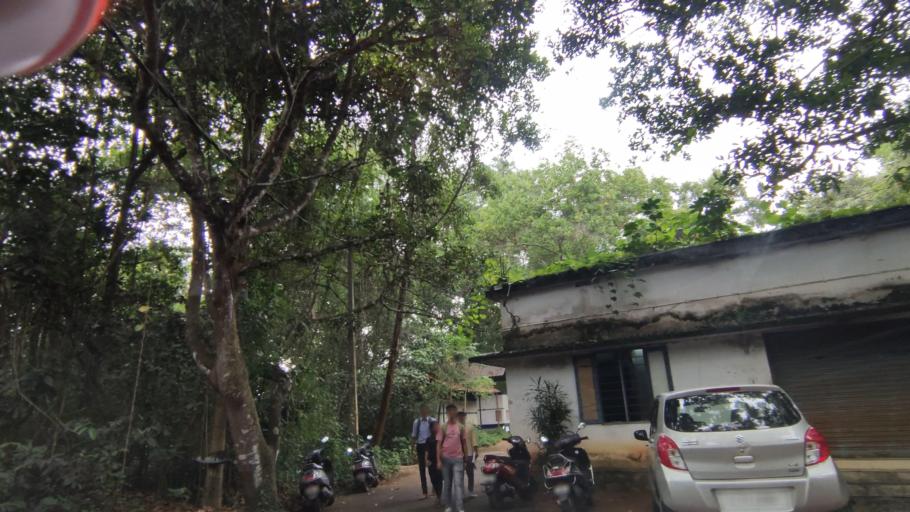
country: IN
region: Kerala
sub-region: Kottayam
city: Kottayam
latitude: 9.6580
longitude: 76.5337
